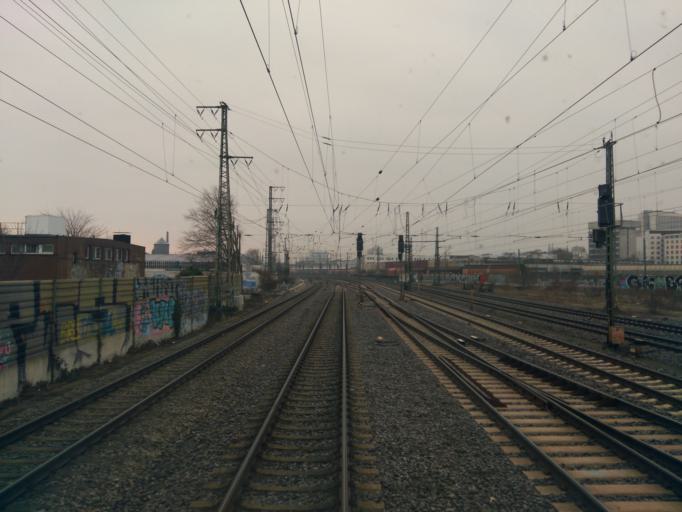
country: DE
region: Bremen
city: Bremen
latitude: 53.0898
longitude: 8.8023
